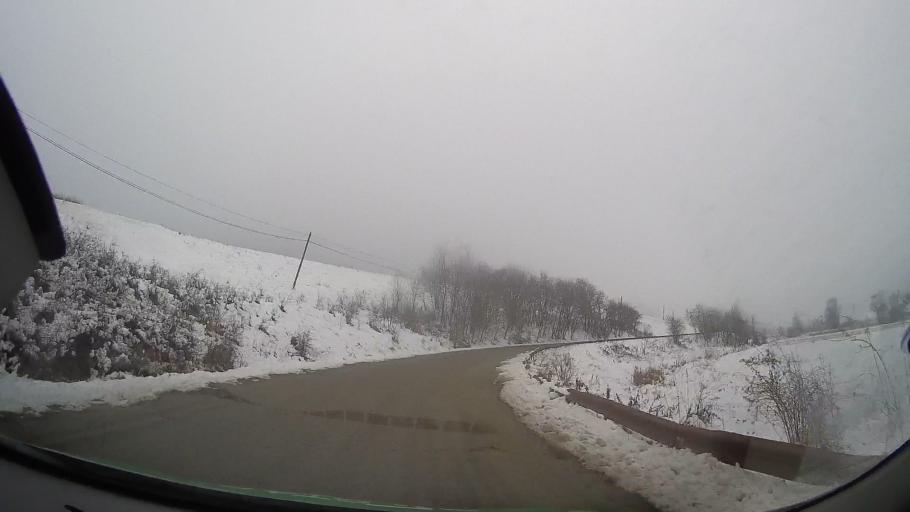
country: RO
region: Bacau
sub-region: Comuna Vultureni
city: Vultureni
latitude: 46.3978
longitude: 27.2771
